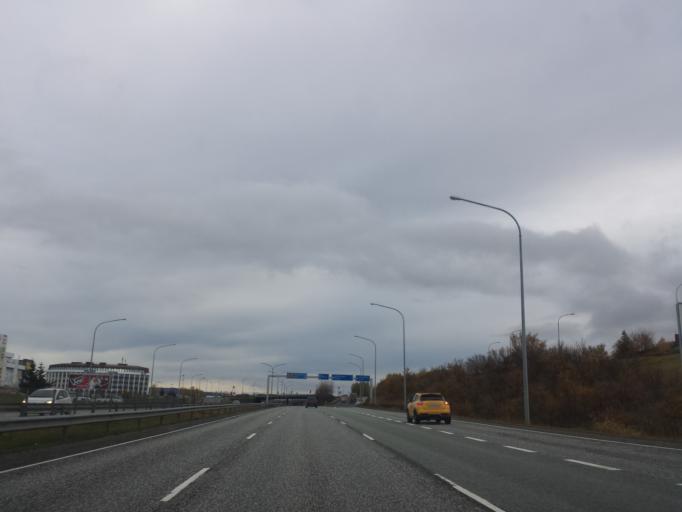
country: IS
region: Capital Region
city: Reykjavik
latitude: 64.1240
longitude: -21.8195
